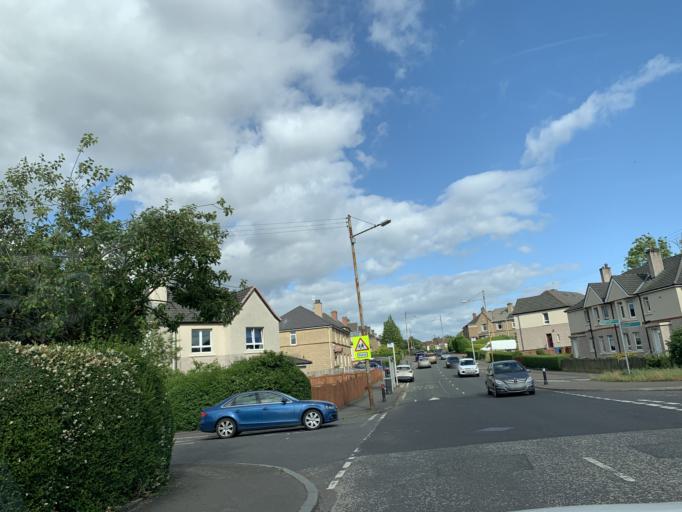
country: GB
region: Scotland
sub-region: Renfrewshire
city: Renfrew
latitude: 55.8516
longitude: -4.3464
